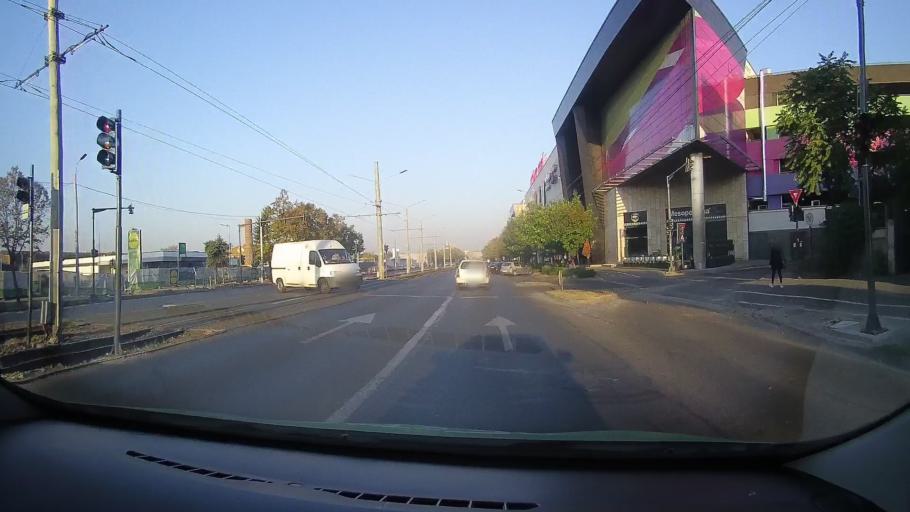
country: RO
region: Arad
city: Arad
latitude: 46.1896
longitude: 21.3216
